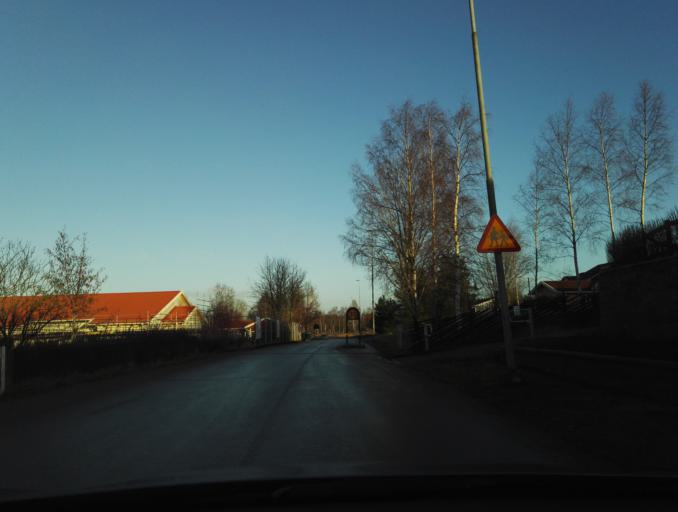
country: SE
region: Kronoberg
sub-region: Vaxjo Kommun
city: Vaexjoe
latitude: 56.9054
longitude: 14.7992
